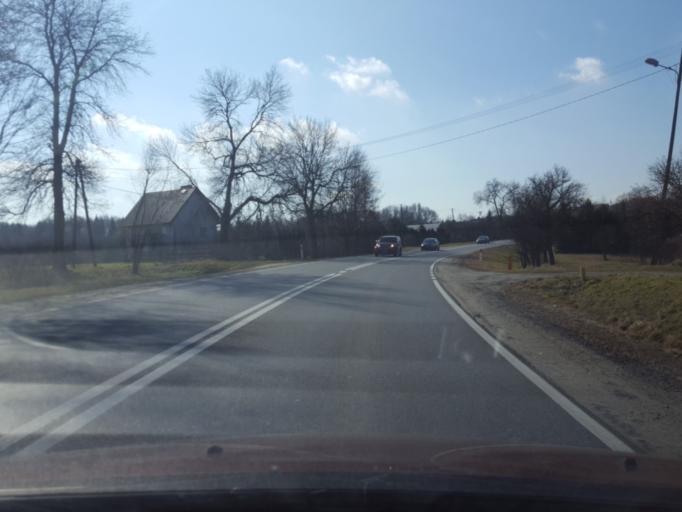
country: PL
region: Lesser Poland Voivodeship
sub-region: Powiat brzeski
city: Gnojnik
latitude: 49.8788
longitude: 20.6176
